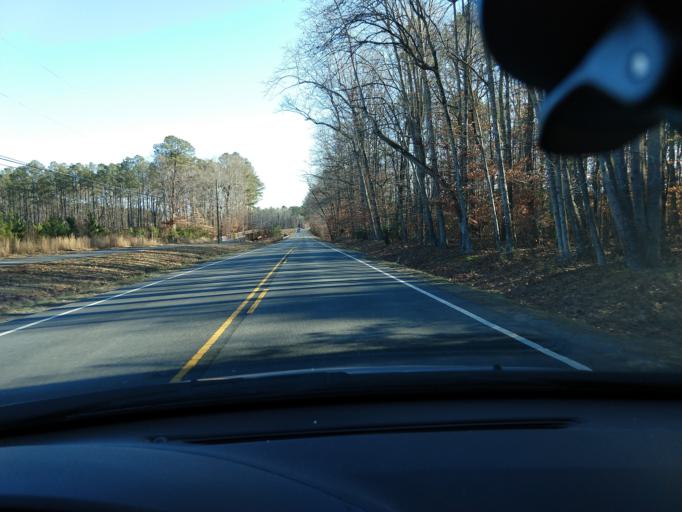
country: US
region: Virginia
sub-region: Charles City County
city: Charles City
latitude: 37.3203
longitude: -76.9730
